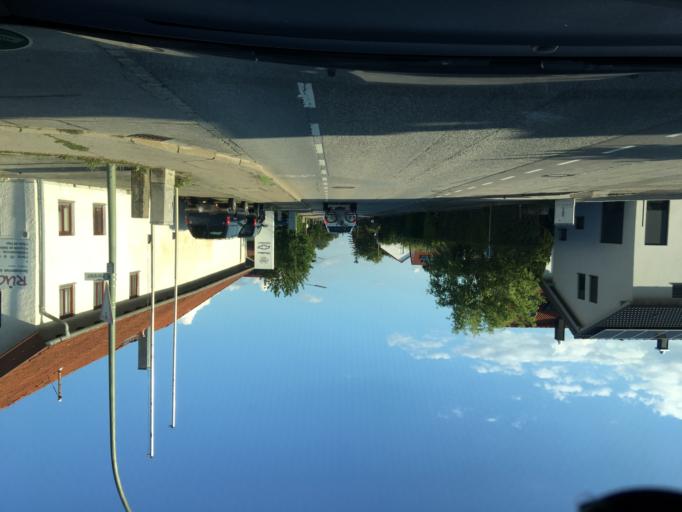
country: DE
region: Bavaria
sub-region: Upper Bavaria
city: Erding
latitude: 48.3155
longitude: 11.9218
